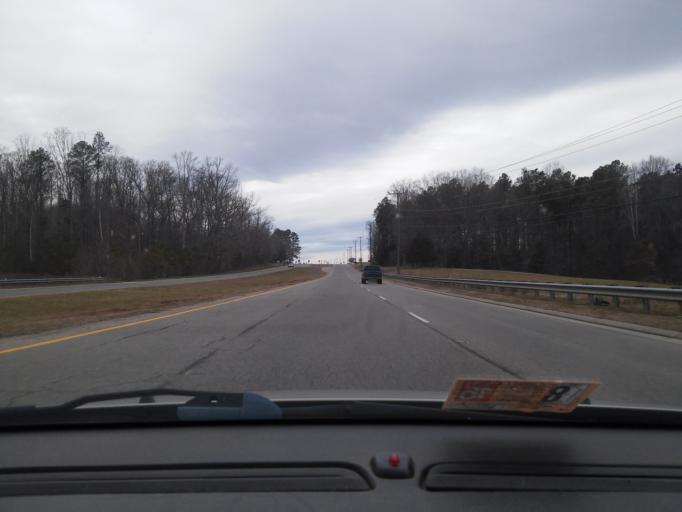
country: US
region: Virginia
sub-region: Henrico County
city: Short Pump
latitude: 37.6666
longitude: -77.6655
